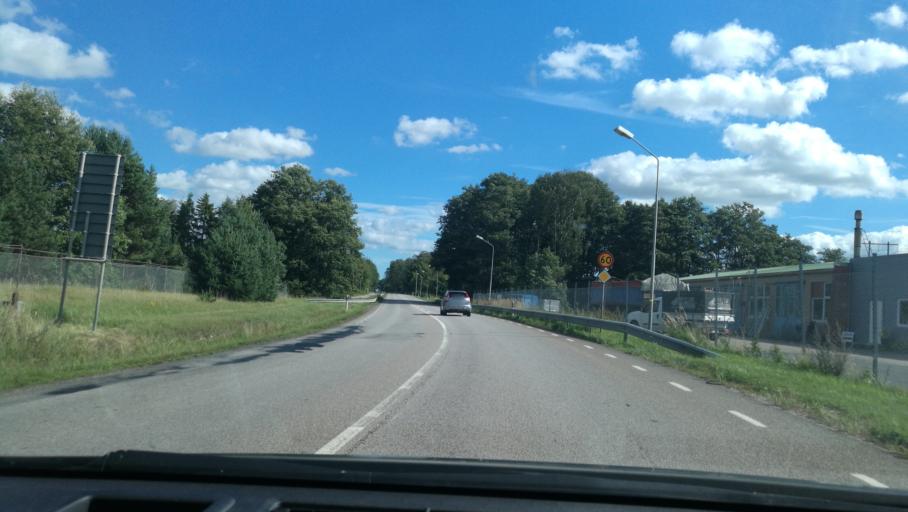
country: SE
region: Vaestra Goetaland
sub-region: Lidkopings Kommun
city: Vinninga
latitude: 58.4914
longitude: 13.2356
